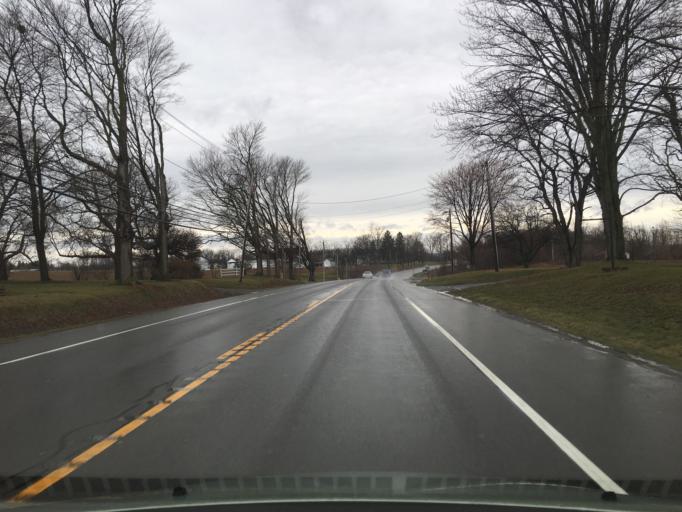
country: US
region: New York
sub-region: Livingston County
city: Avon
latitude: 42.9092
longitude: -77.7221
